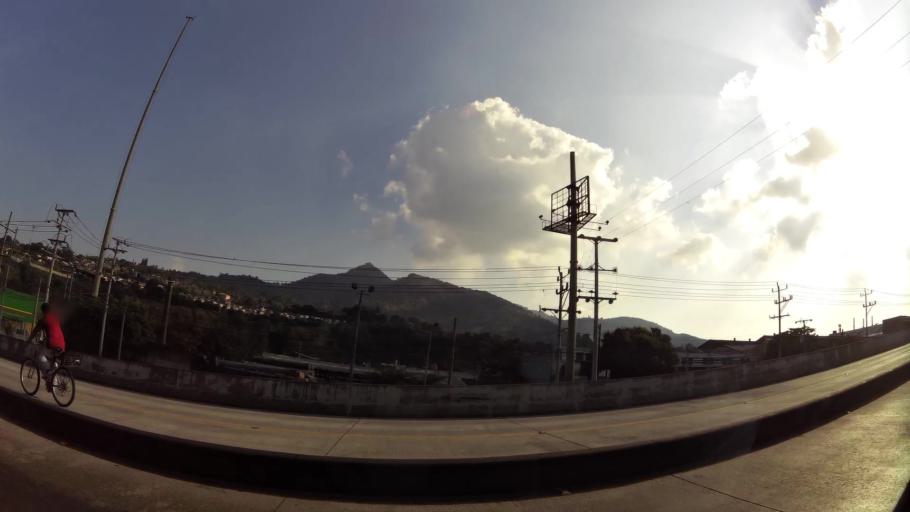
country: SV
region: San Salvador
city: San Salvador
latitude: 13.7007
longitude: -89.1676
